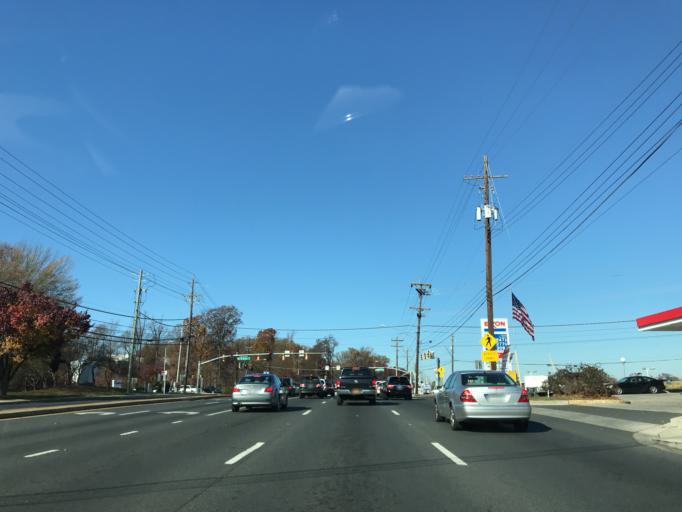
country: US
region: Maryland
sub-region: Montgomery County
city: Derwood
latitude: 39.1056
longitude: -77.1575
